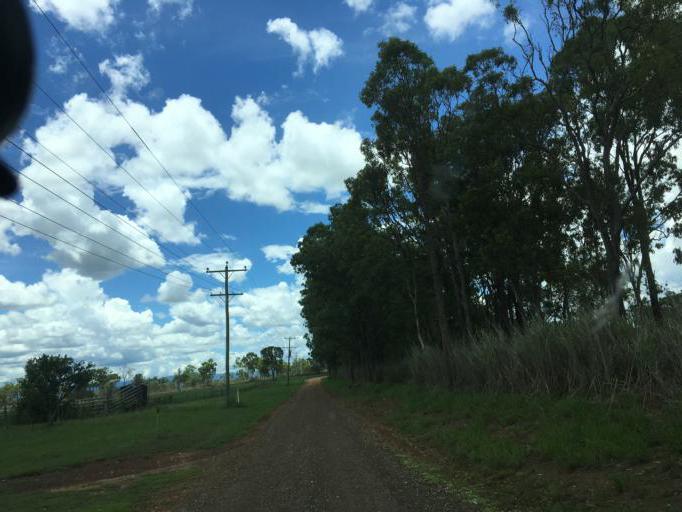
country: AU
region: Queensland
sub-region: Tablelands
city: Mareeba
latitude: -16.9912
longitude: 145.5228
